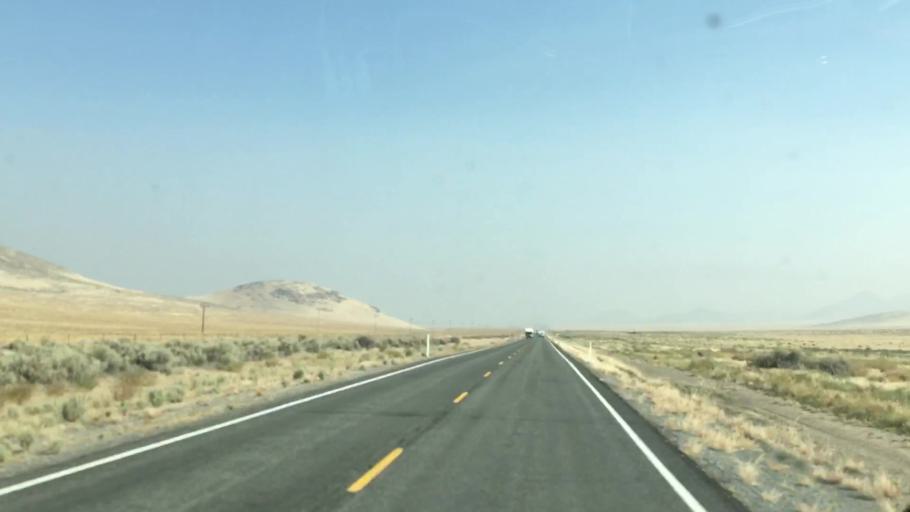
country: US
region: Nevada
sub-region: Lyon County
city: Fernley
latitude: 40.4245
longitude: -119.3339
